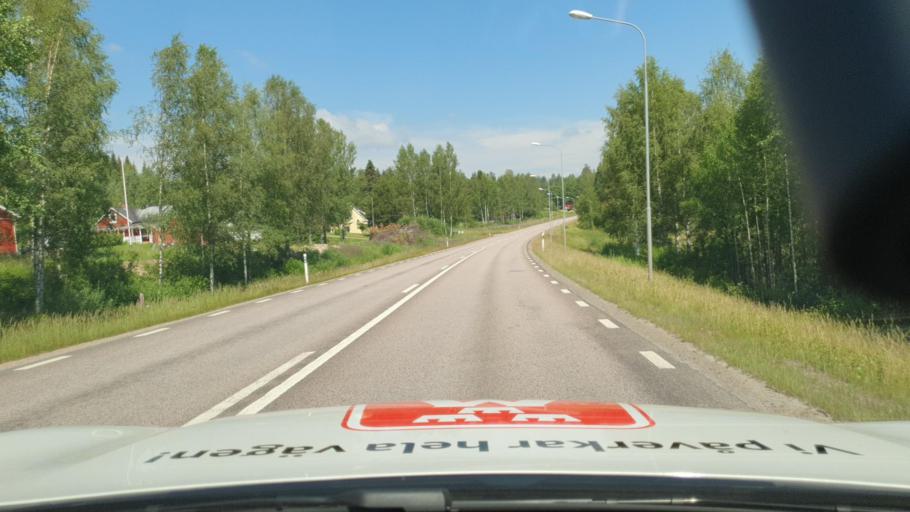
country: SE
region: Vaermland
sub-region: Torsby Kommun
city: Torsby
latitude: 60.1735
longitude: 13.0058
